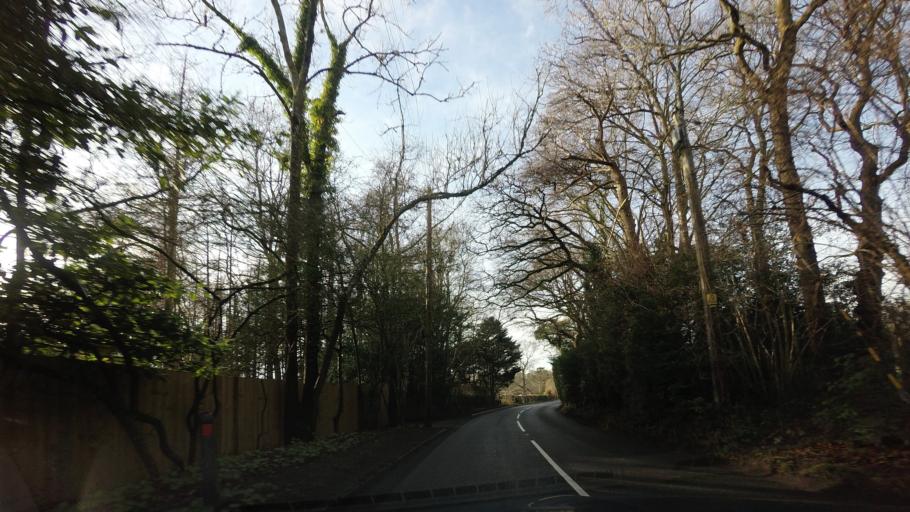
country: GB
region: England
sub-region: East Sussex
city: Battle
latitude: 50.9011
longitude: 0.4600
